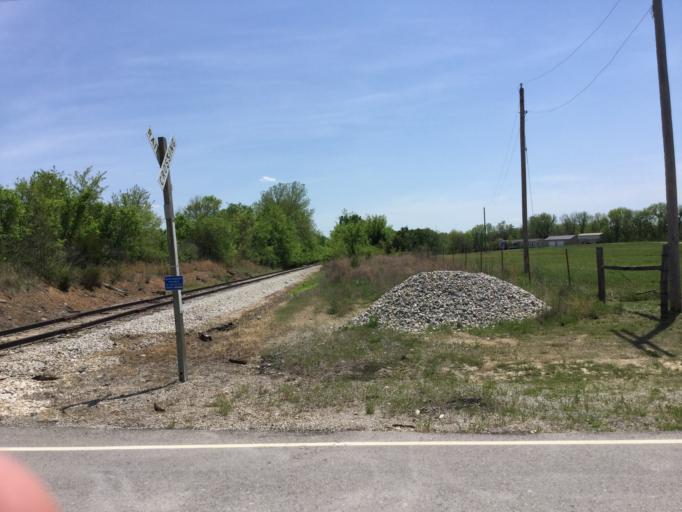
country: US
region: Kansas
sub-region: Montgomery County
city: Cherryvale
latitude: 37.3402
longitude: -95.5893
